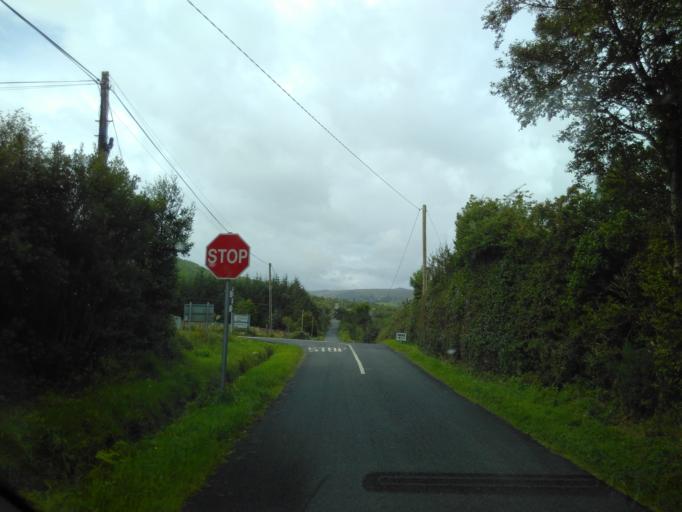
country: IE
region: Ulster
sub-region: County Donegal
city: Dunlewy
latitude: 54.9785
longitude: -7.9302
